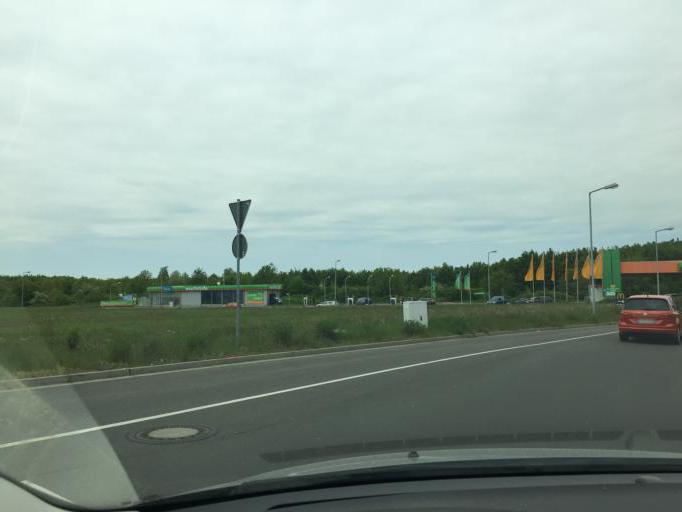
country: DE
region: Saxony
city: Rackwitz
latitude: 51.4024
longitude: 12.3946
